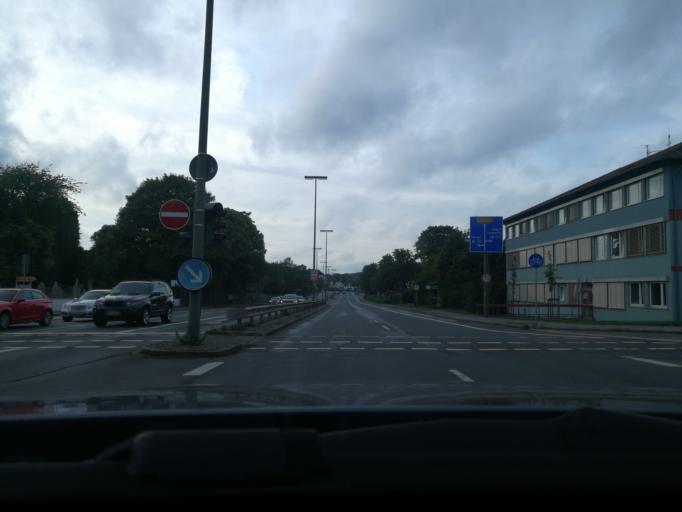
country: DE
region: North Rhine-Westphalia
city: Iserlohn
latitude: 51.3810
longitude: 7.6808
